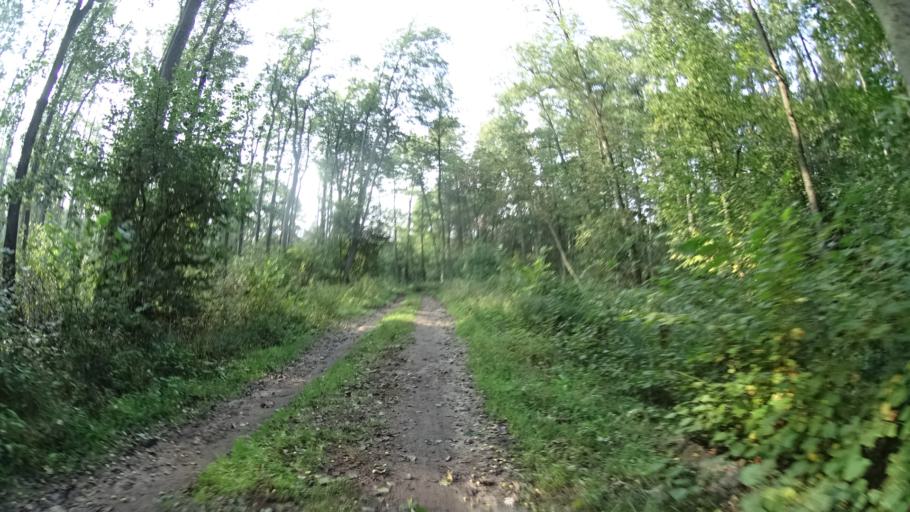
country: DE
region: Lower Saxony
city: Reppenstedt
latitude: 53.2280
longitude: 10.3450
